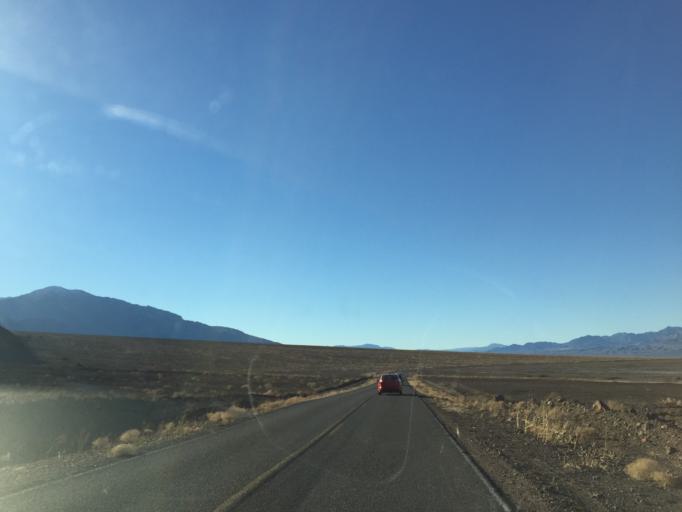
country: US
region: California
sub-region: San Bernardino County
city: Searles Valley
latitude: 36.1424
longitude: -116.7646
